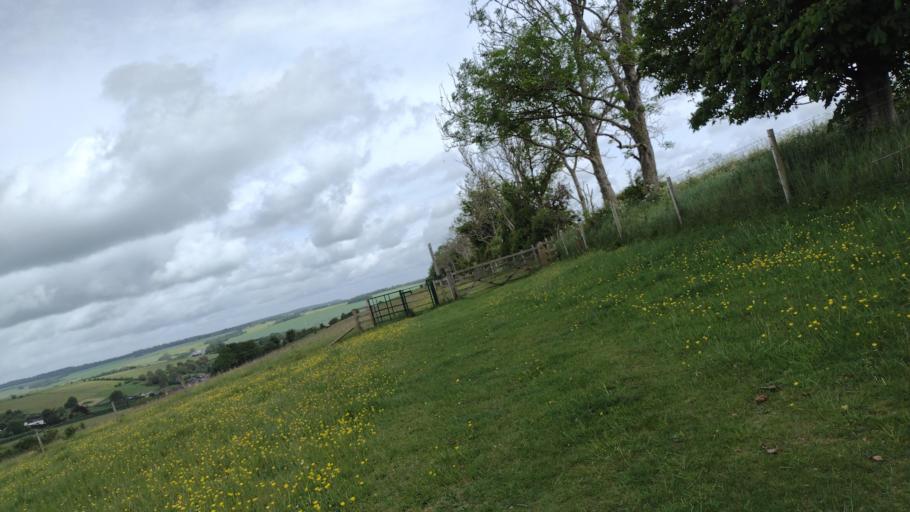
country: GB
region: England
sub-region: Wiltshire
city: Wilton
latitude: 51.0228
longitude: -1.8410
